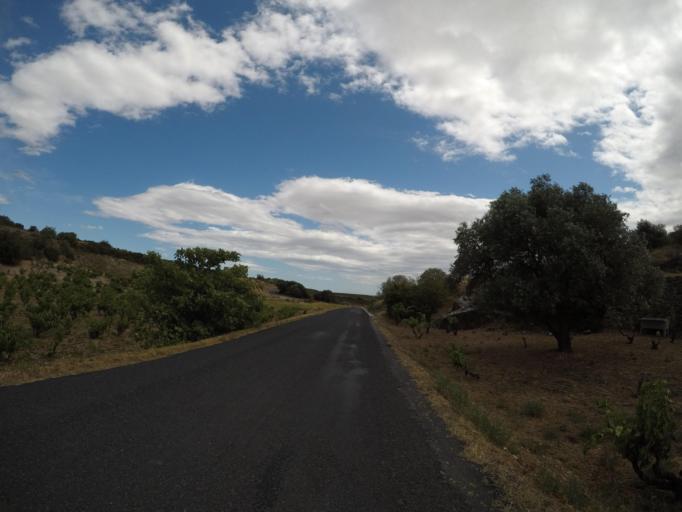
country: FR
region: Languedoc-Roussillon
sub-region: Departement des Pyrenees-Orientales
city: Baixas
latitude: 42.7545
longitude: 2.7734
